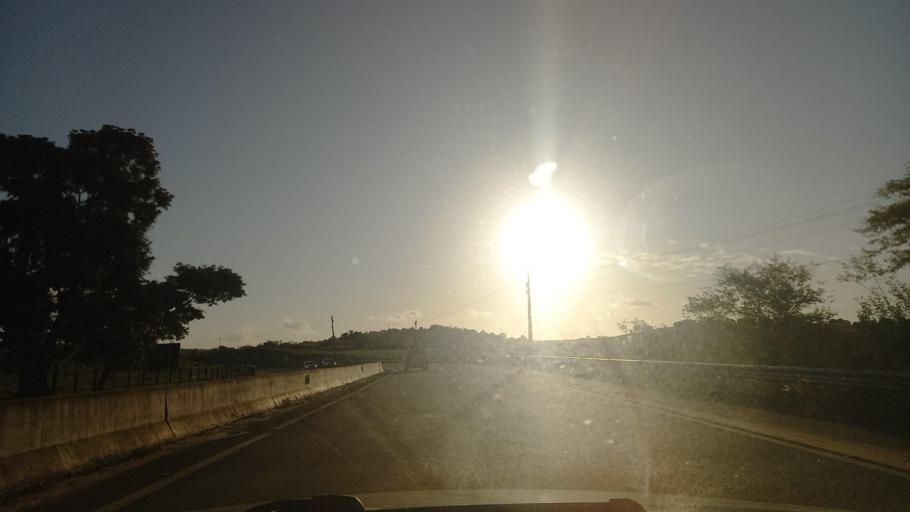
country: BR
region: Alagoas
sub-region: Limoeiro De Anadia
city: Limoeiro de Anadia
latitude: -9.7381
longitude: -36.4878
